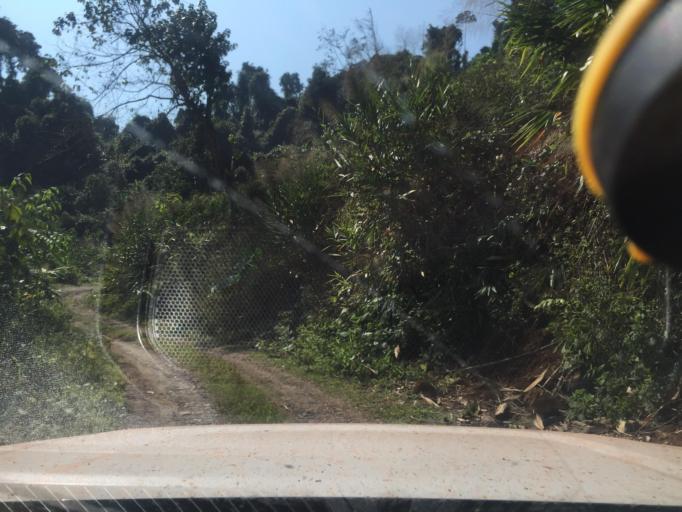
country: LA
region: Phongsali
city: Phongsali
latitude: 21.6547
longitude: 102.4146
